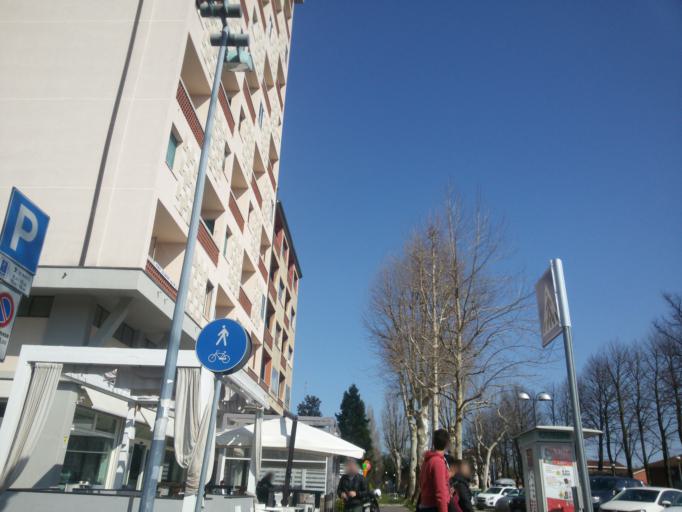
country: IT
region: Emilia-Romagna
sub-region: Provincia di Ravenna
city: Lugo
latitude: 44.4147
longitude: 11.9144
